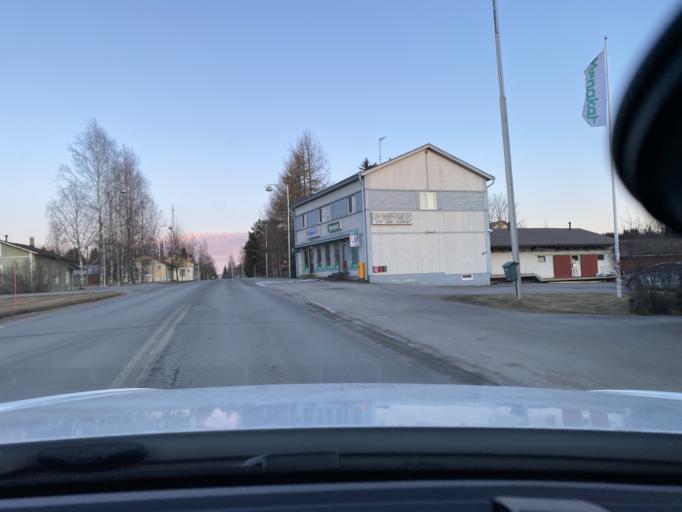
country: FI
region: Pirkanmaa
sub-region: Lounais-Pirkanmaa
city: Punkalaidun
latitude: 61.1176
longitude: 23.0852
